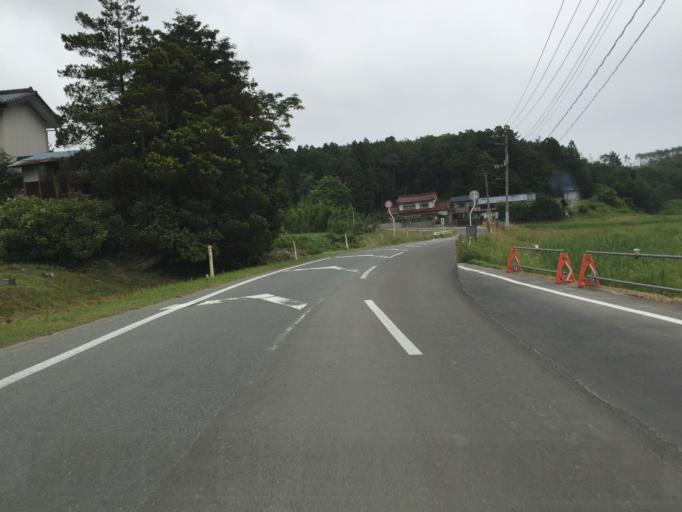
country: JP
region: Fukushima
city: Namie
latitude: 37.7316
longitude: 141.0068
